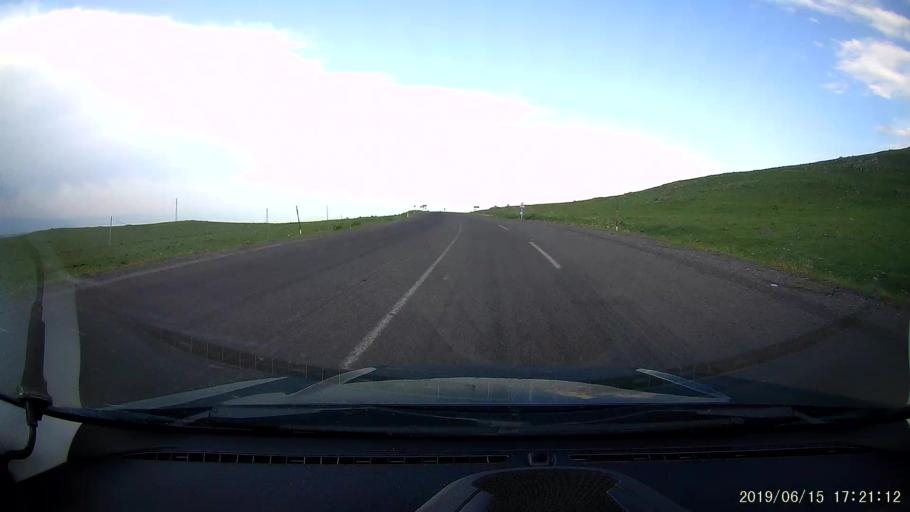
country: TR
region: Kars
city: Basgedikler
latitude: 40.6174
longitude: 43.3203
